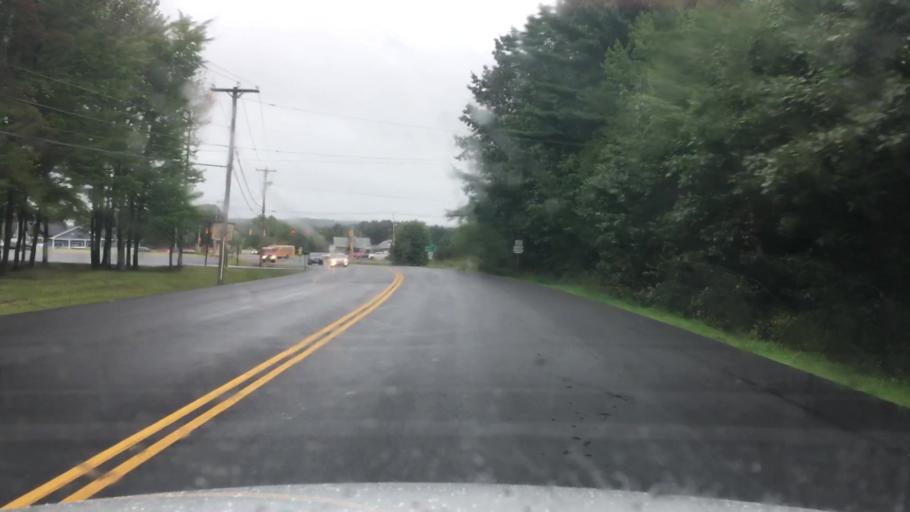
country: US
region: Maine
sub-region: Penobscot County
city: Hampden
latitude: 44.7555
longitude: -68.8417
